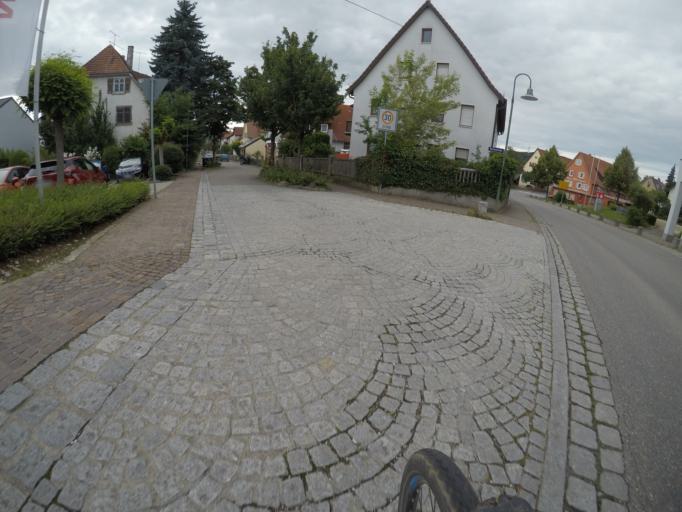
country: DE
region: Baden-Wuerttemberg
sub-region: Regierungsbezirk Stuttgart
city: Bempflingen
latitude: 48.5713
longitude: 9.2685
